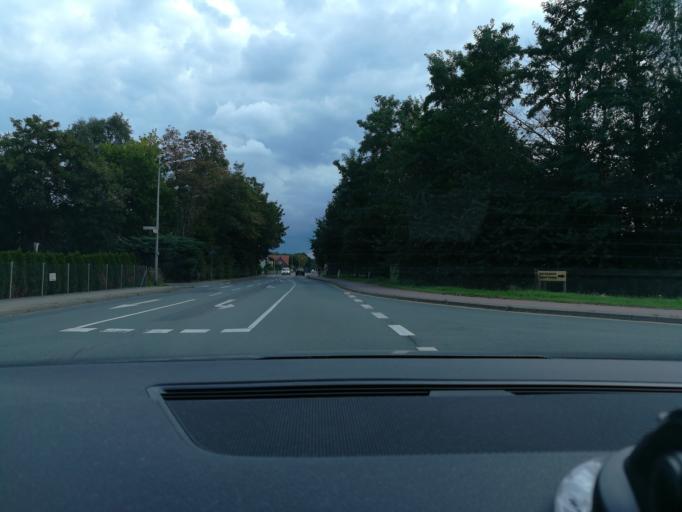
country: DE
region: North Rhine-Westphalia
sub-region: Regierungsbezirk Detmold
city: Minden
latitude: 52.3217
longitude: 8.8721
